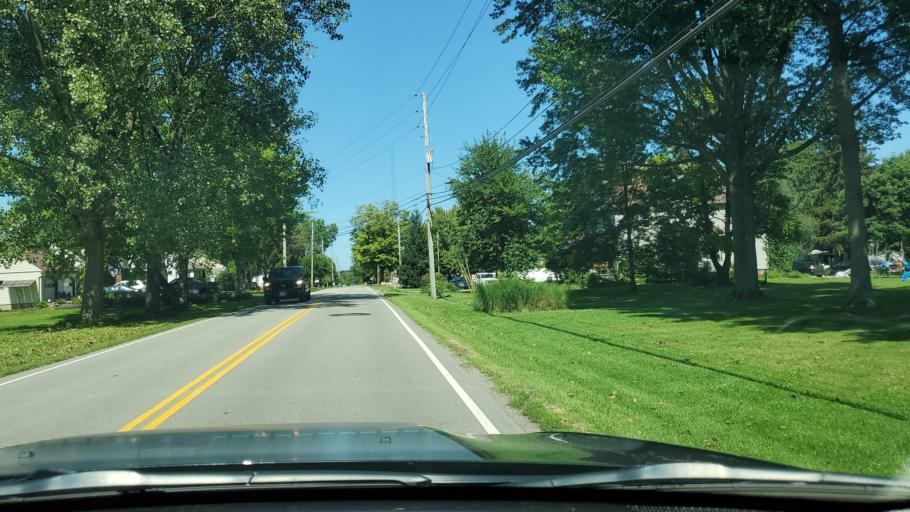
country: US
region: Ohio
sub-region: Trumbull County
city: McKinley Heights
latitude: 41.1799
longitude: -80.6919
